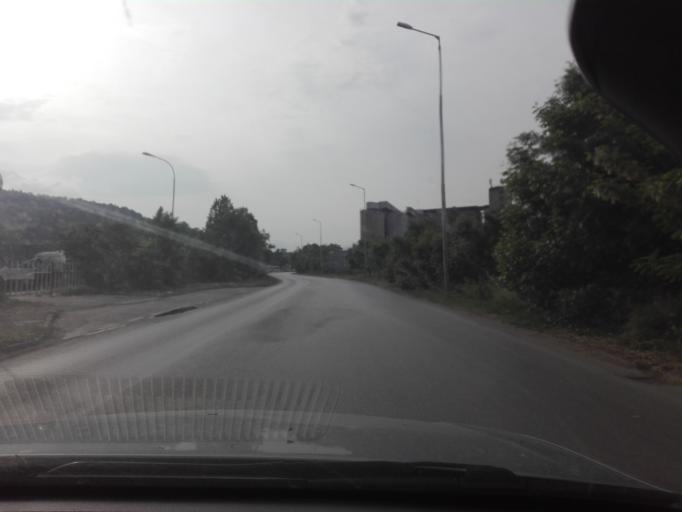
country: MK
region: Bitola
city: Bitola
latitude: 41.0139
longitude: 21.3473
